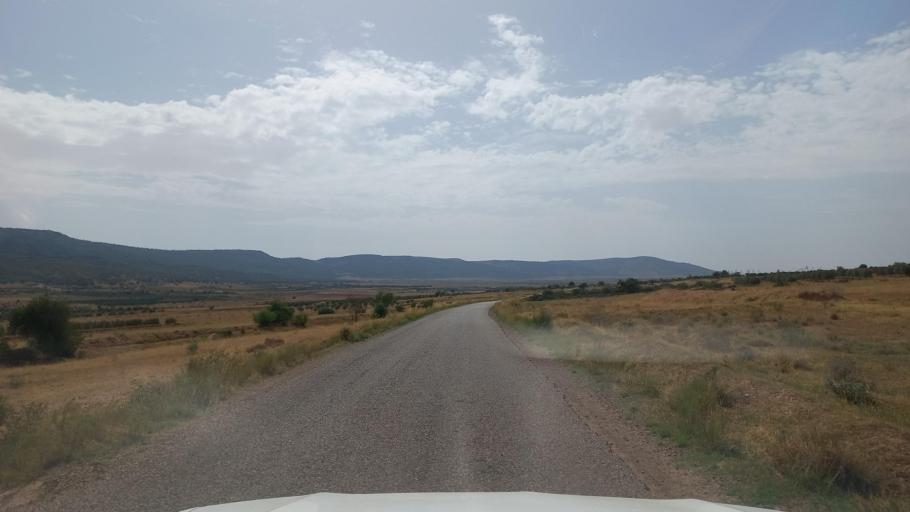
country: TN
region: Al Qasrayn
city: Kasserine
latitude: 35.3683
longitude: 8.8842
